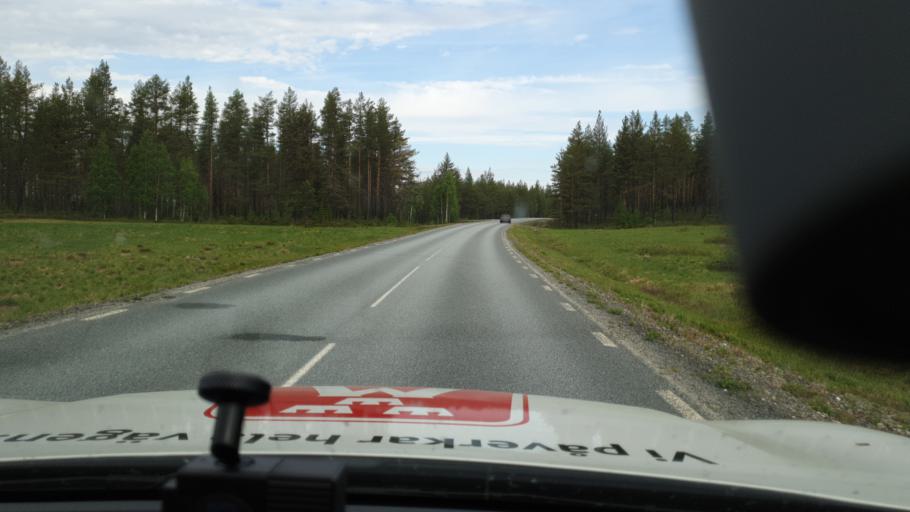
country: SE
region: Vaesterbotten
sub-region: Mala Kommun
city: Mala
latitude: 65.0021
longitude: 18.4698
